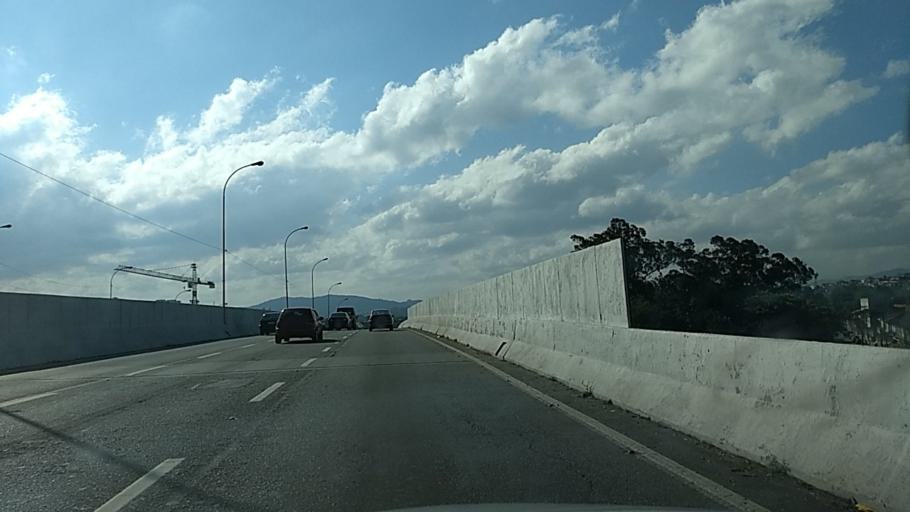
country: BR
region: Sao Paulo
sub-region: Osasco
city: Osasco
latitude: -23.5298
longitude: -46.7735
